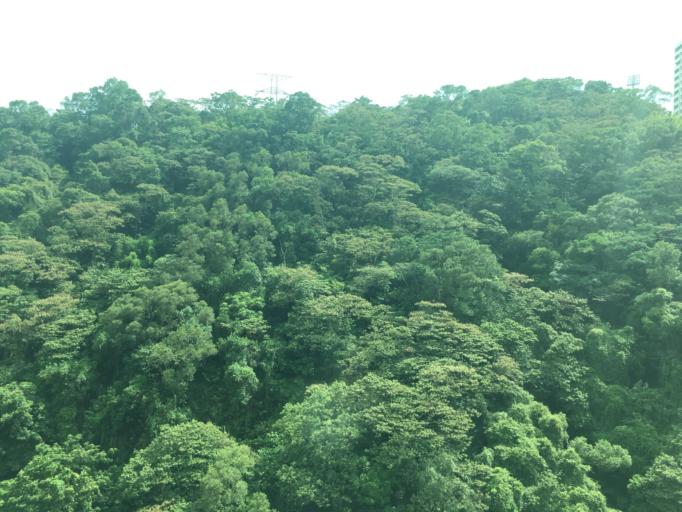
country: TW
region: Taipei
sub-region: Taipei
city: Banqiao
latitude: 25.0334
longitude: 121.3951
